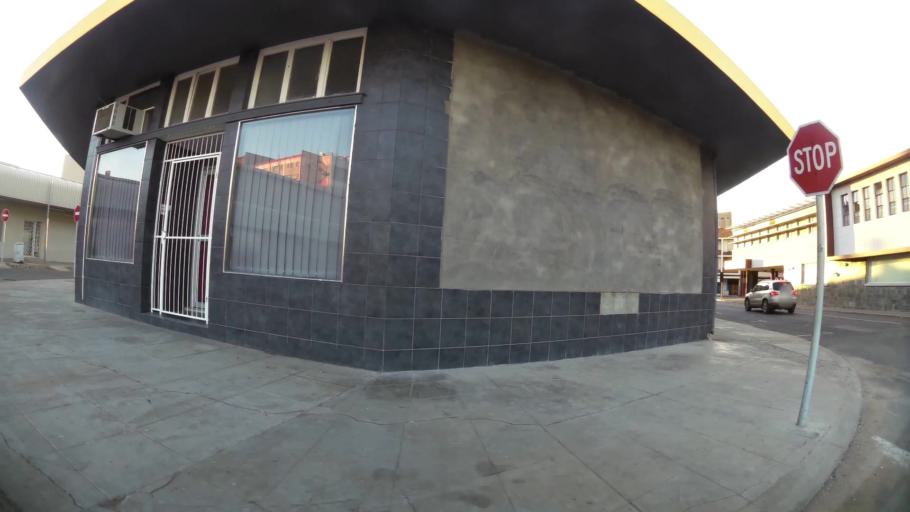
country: ZA
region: Northern Cape
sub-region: Frances Baard District Municipality
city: Kimberley
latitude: -28.7392
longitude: 24.7666
